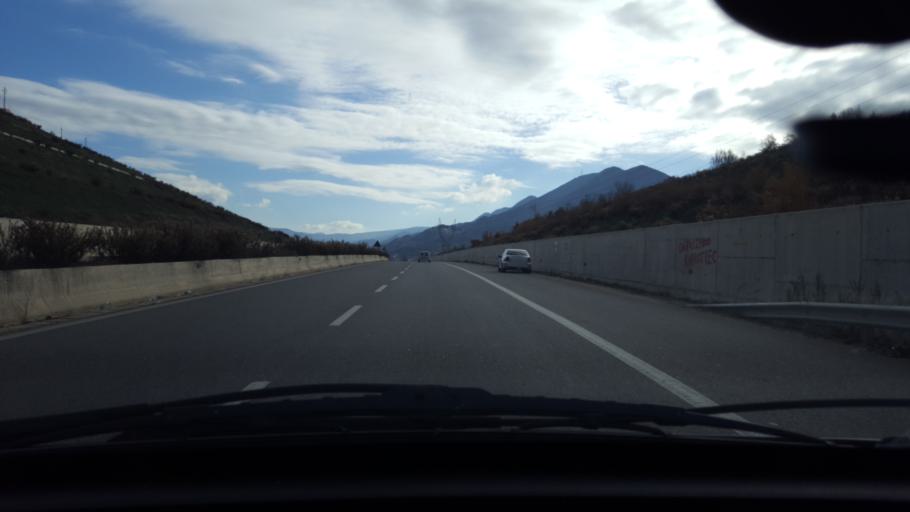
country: AL
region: Tirane
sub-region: Rrethi i Tiranes
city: Petrele
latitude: 41.2697
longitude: 19.8621
